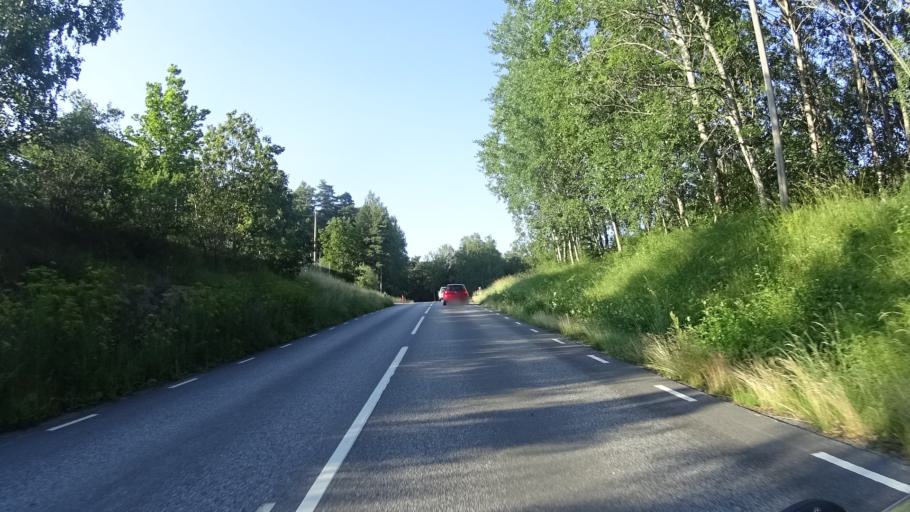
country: SE
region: Stockholm
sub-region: Sodertalje Kommun
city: Pershagen
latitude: 59.1038
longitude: 17.6341
